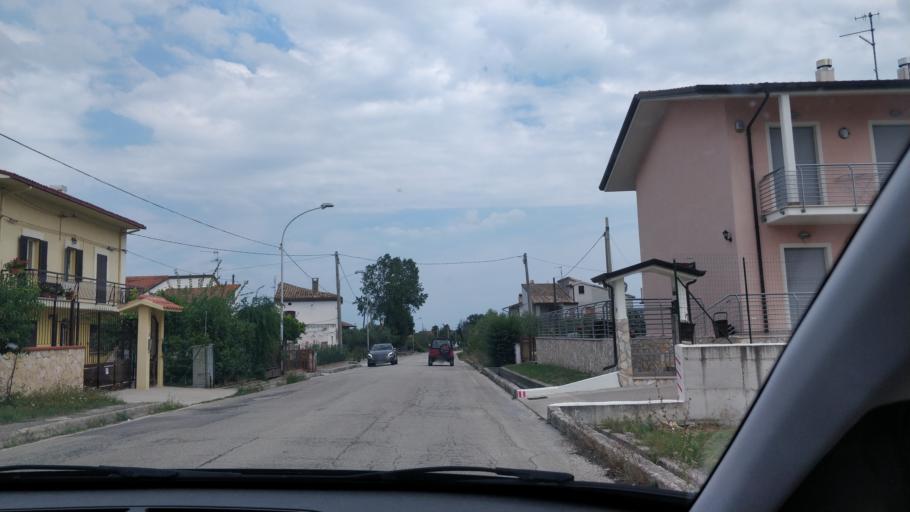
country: IT
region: Abruzzo
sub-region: Provincia di Chieti
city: San Vito Chietino
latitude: 42.2817
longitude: 14.4385
